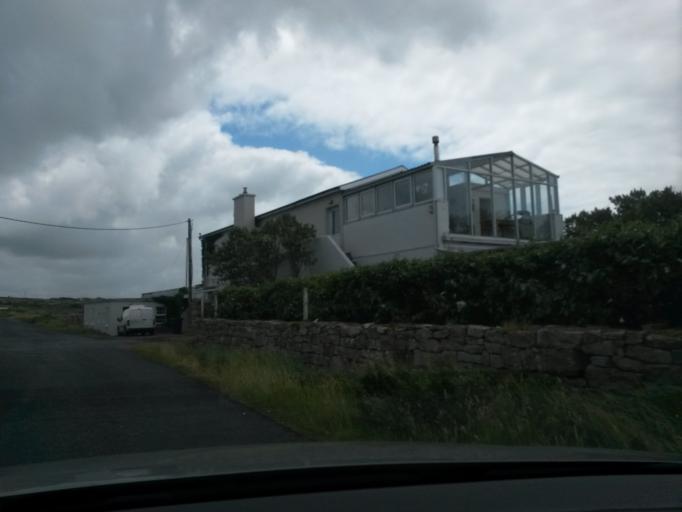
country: IE
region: Connaught
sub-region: County Galway
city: Oughterard
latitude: 53.2459
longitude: -9.5486
